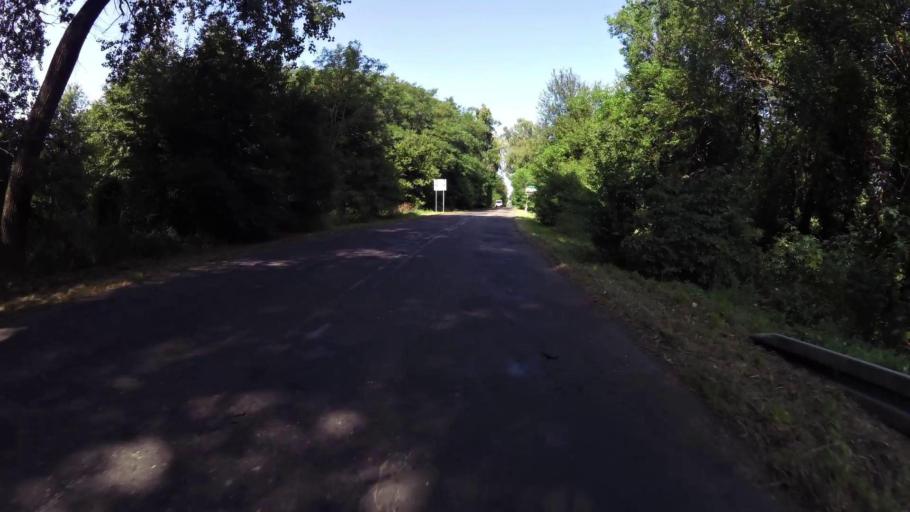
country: PL
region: West Pomeranian Voivodeship
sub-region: Powiat stargardzki
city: Dobrzany
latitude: 53.3350
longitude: 15.3931
